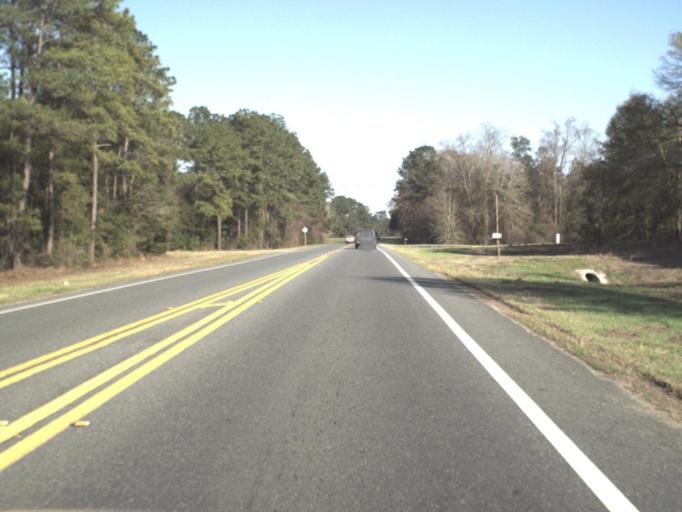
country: US
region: Florida
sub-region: Jackson County
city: Marianna
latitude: 30.7459
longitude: -85.1708
